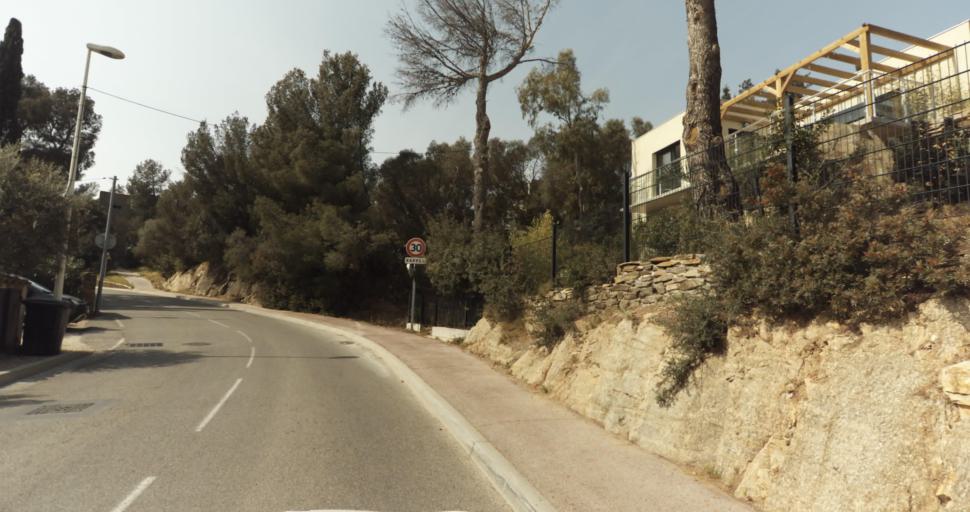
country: FR
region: Provence-Alpes-Cote d'Azur
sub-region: Departement du Var
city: Bormes-les-Mimosas
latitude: 43.1443
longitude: 6.3489
